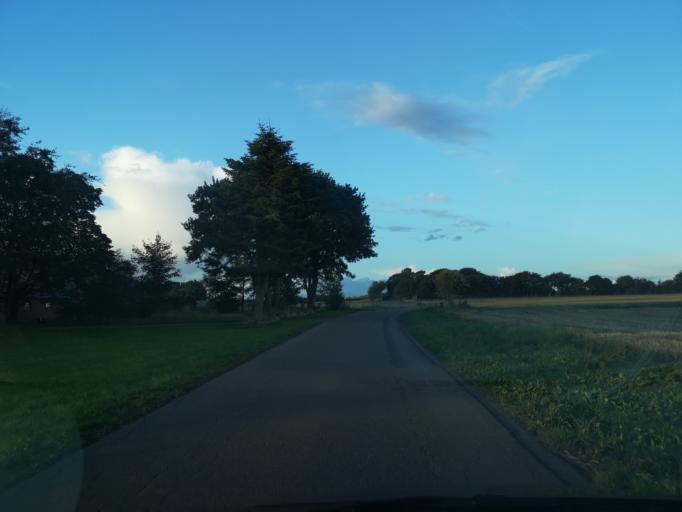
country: DK
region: Central Jutland
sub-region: Ringkobing-Skjern Kommune
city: Videbaek
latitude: 56.0280
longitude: 8.5650
